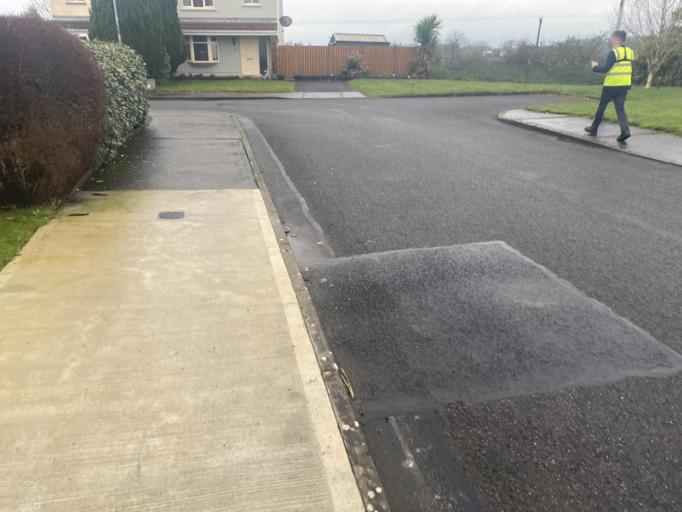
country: IE
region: Connaught
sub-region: County Galway
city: Tuam
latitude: 53.5200
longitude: -8.8376
